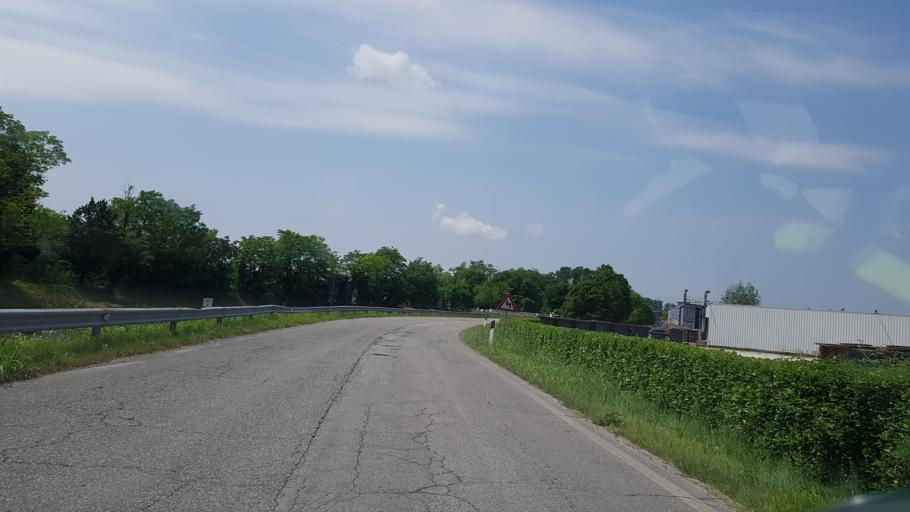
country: IT
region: Friuli Venezia Giulia
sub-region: Provincia di Udine
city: Torreano
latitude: 46.1168
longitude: 13.4166
